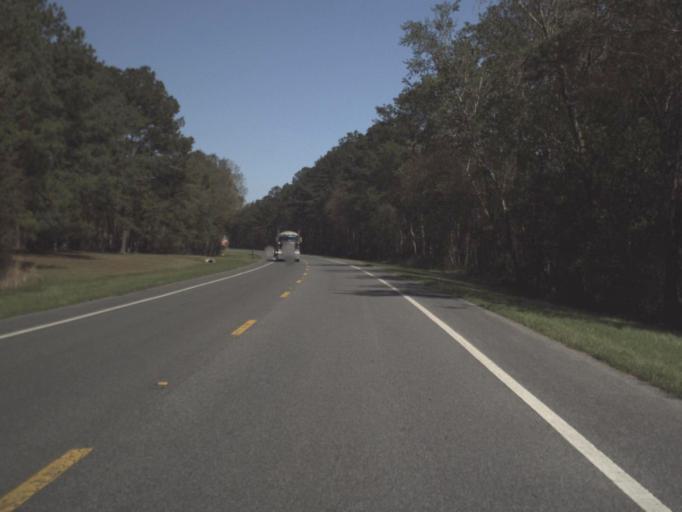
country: US
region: Florida
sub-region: Walton County
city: DeFuniak Springs
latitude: 30.7226
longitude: -85.9482
